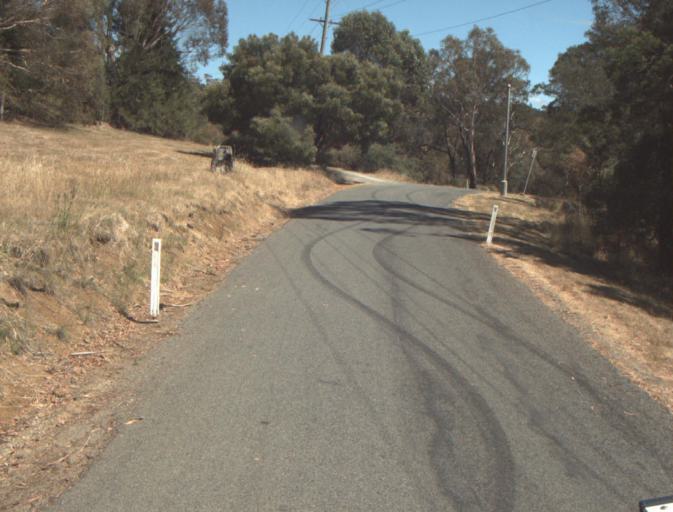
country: AU
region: Tasmania
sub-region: Launceston
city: Summerhill
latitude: -41.4594
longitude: 147.1177
